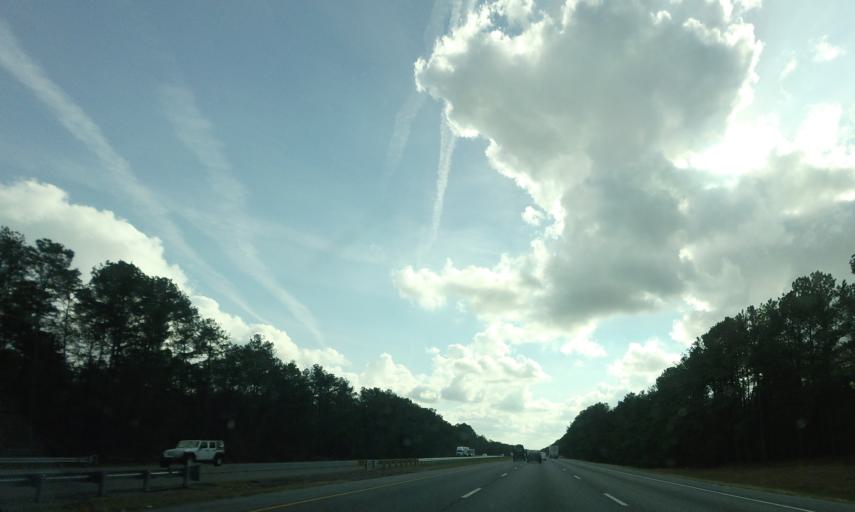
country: US
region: Georgia
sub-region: Houston County
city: Perry
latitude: 32.3813
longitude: -83.7682
